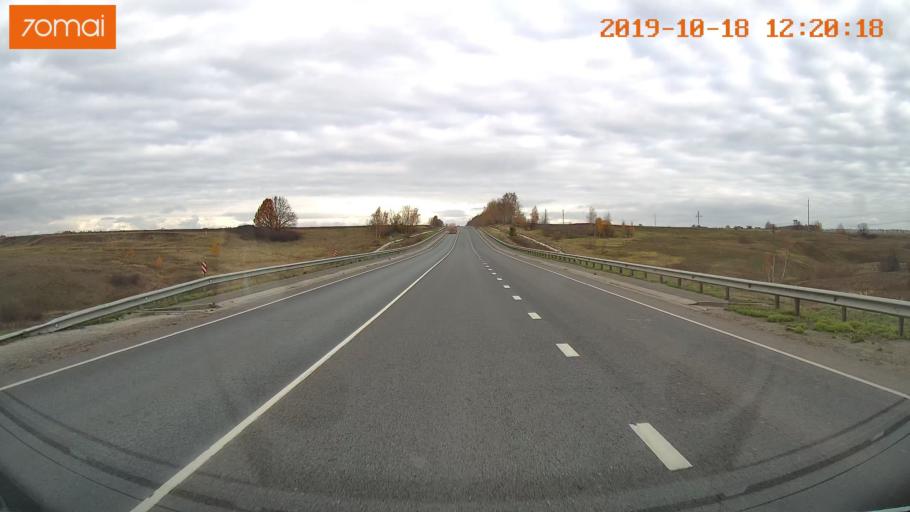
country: RU
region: Rjazan
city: Bagramovo
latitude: 54.4956
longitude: 39.4786
